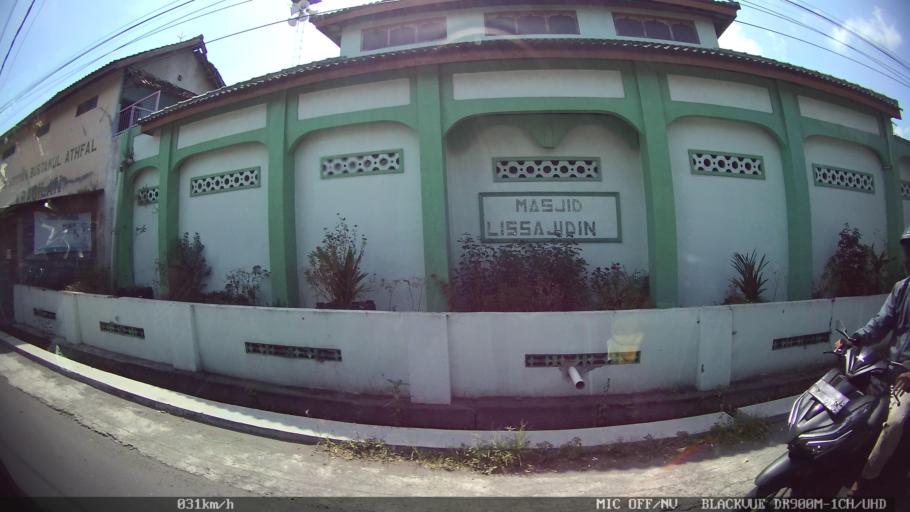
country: ID
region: Daerah Istimewa Yogyakarta
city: Sewon
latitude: -7.8311
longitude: 110.3805
